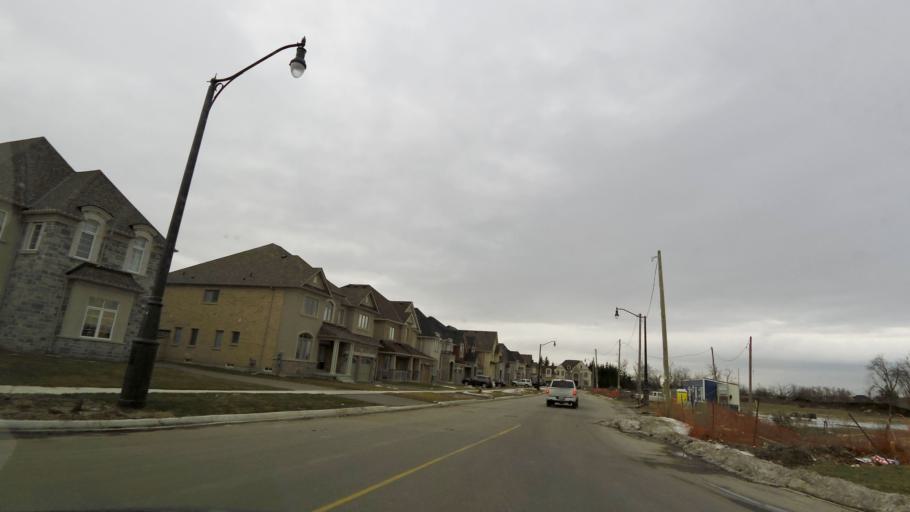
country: CA
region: Ontario
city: Brampton
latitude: 43.7876
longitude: -79.7435
